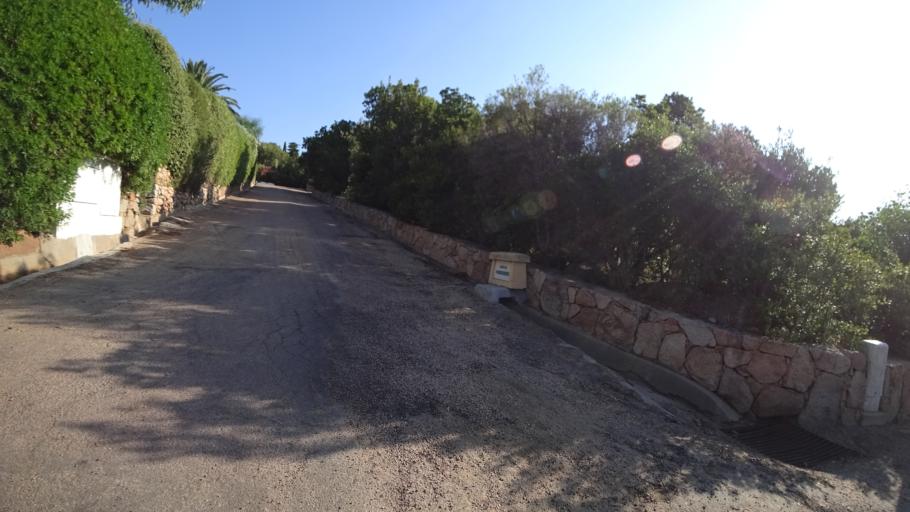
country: FR
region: Corsica
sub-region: Departement de la Corse-du-Sud
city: Porto-Vecchio
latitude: 41.6196
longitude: 9.3513
